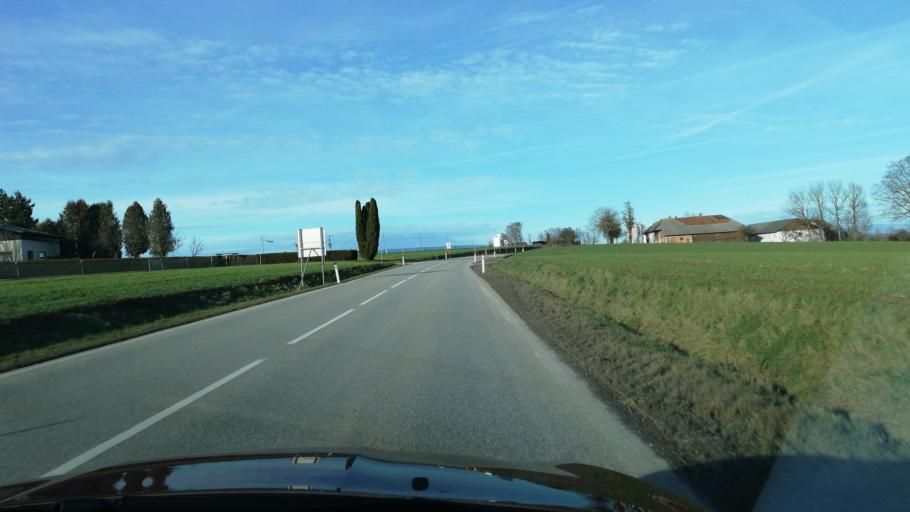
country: AT
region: Upper Austria
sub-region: Politischer Bezirk Kirchdorf an der Krems
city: Kremsmunster
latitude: 47.9824
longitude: 14.0798
